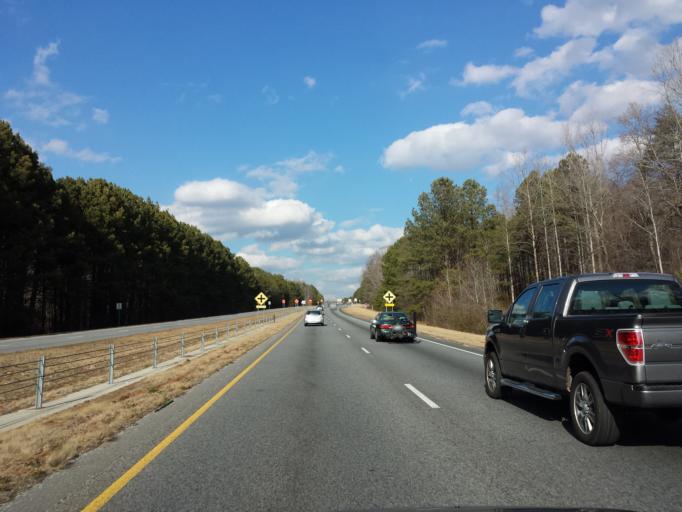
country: US
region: Georgia
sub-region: Dawson County
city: Dawsonville
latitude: 34.3713
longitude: -84.0299
